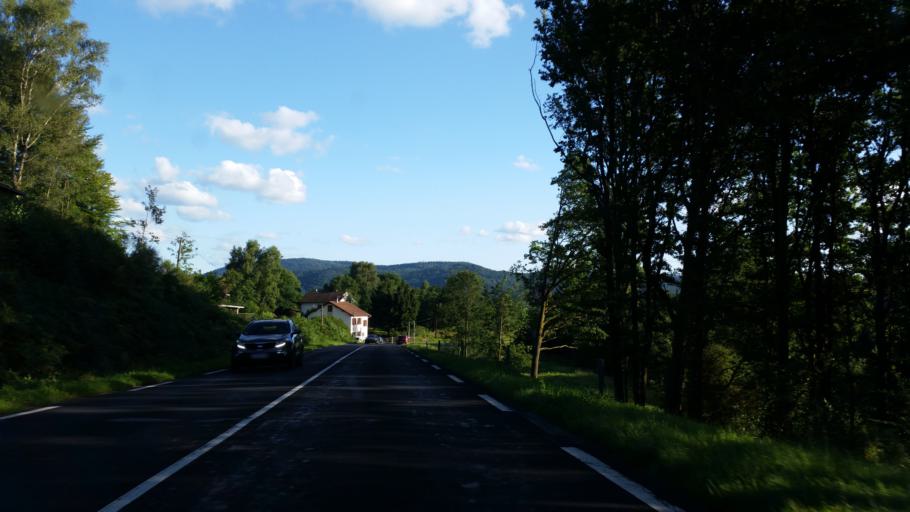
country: FR
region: Lorraine
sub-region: Departement des Vosges
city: Saint-Ame
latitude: 48.0426
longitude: 6.6811
